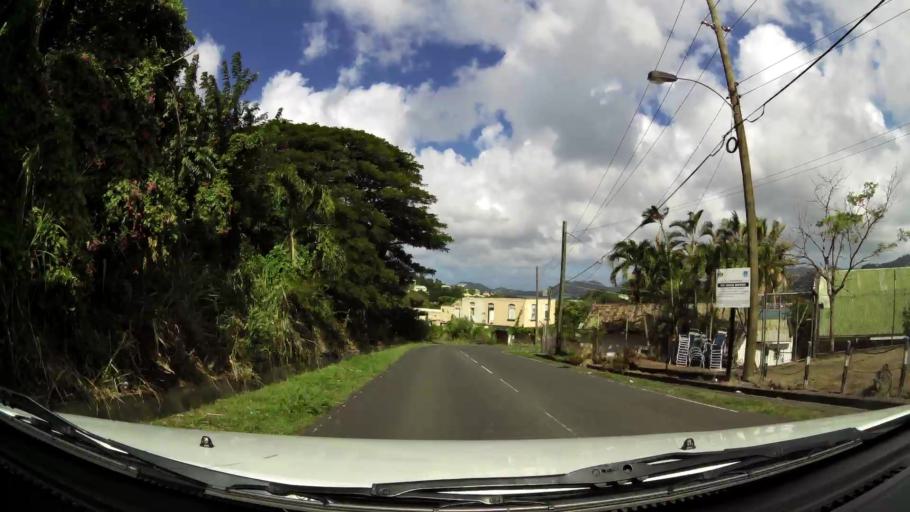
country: LC
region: Castries Quarter
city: Castries
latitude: 14.0131
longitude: -61.0031
